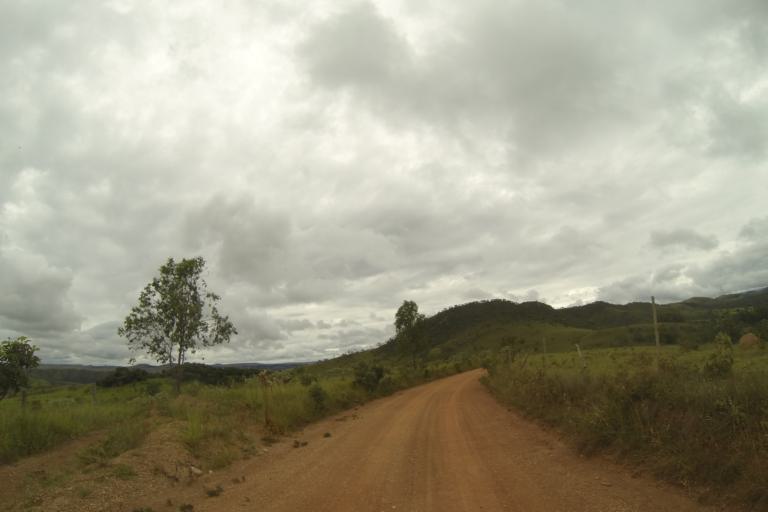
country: BR
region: Minas Gerais
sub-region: Ibia
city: Ibia
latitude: -19.7532
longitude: -46.4965
